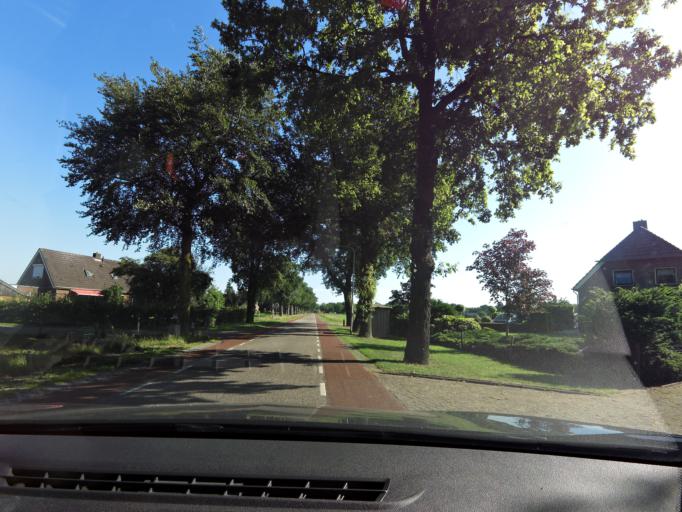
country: NL
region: Overijssel
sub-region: Gemeente Raalte
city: Raalte
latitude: 52.3659
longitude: 6.3958
